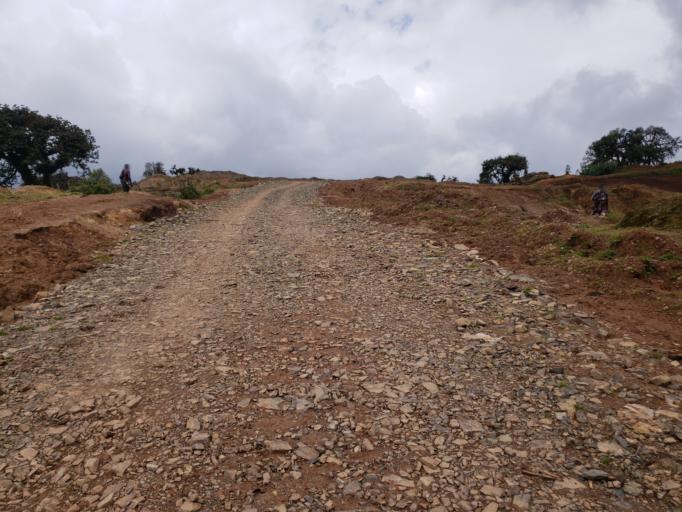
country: ET
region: Oromiya
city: Dodola
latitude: 6.6509
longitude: 39.3623
